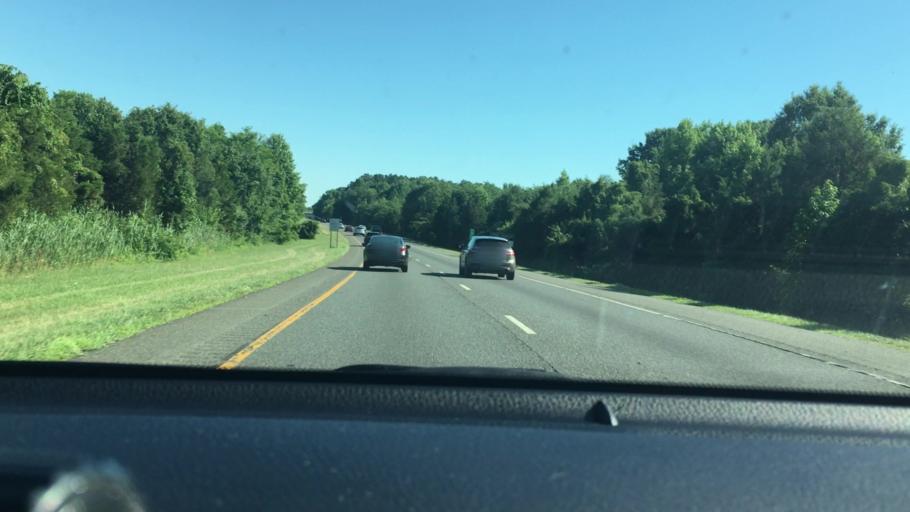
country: US
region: New Jersey
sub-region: Gloucester County
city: Wenonah
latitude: 39.7882
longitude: -75.1167
